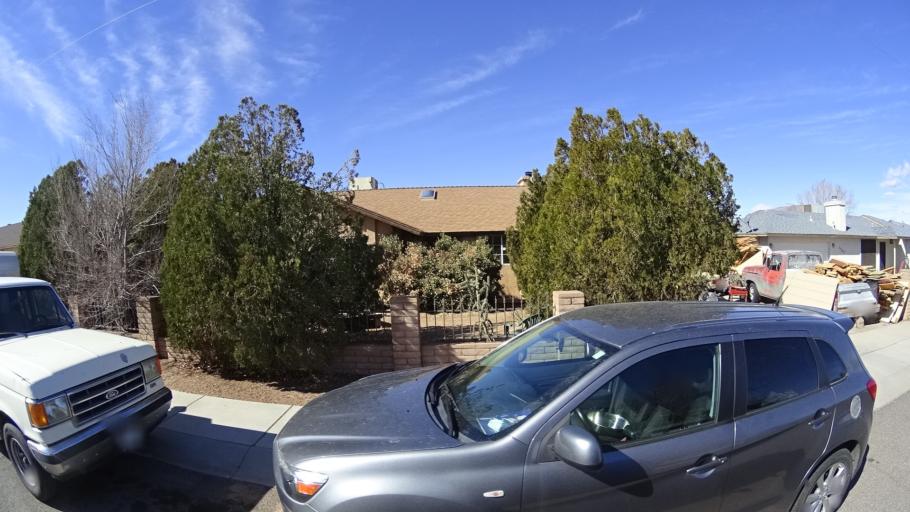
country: US
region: Arizona
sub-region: Mohave County
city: New Kingman-Butler
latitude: 35.2308
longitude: -114.0191
